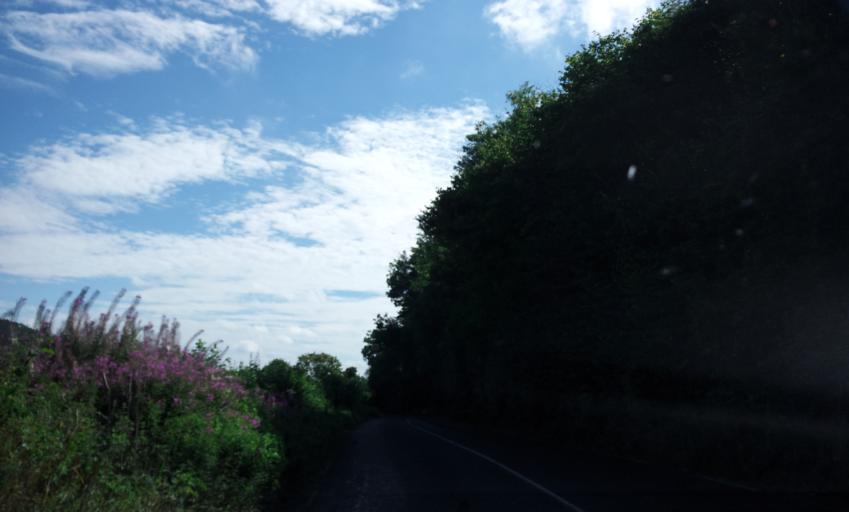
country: IE
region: Leinster
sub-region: Laois
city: Portlaoise
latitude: 53.0122
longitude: -7.2449
